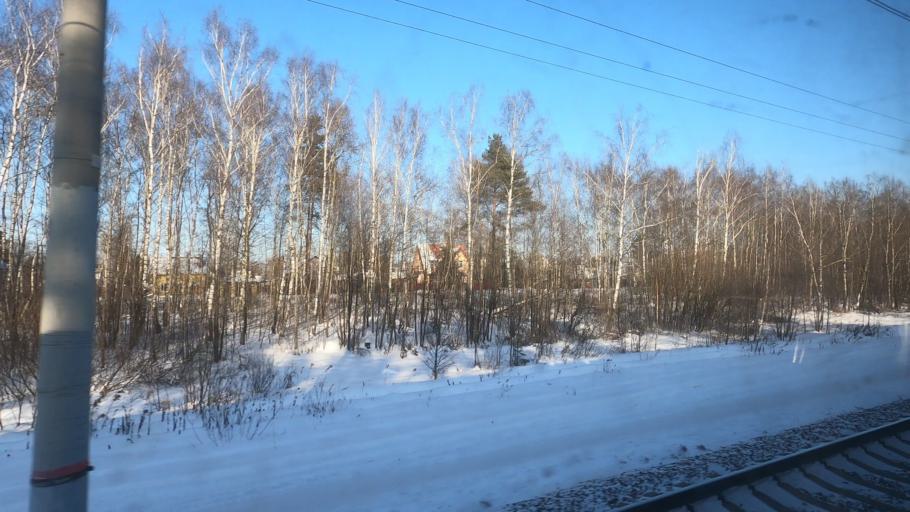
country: RU
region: Moskovskaya
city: Imeni Vorovskogo
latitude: 55.7219
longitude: 38.3054
